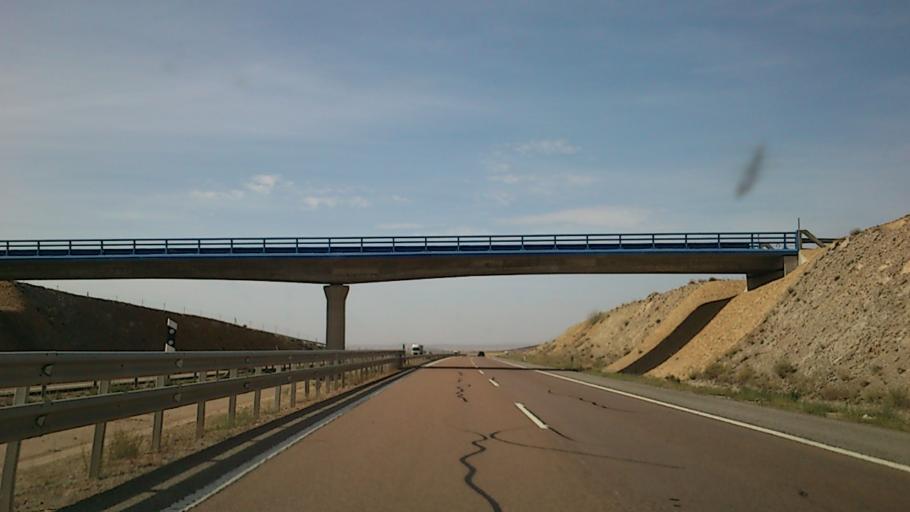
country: ES
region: Aragon
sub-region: Provincia de Teruel
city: Singra
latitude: 40.6399
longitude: -1.3133
